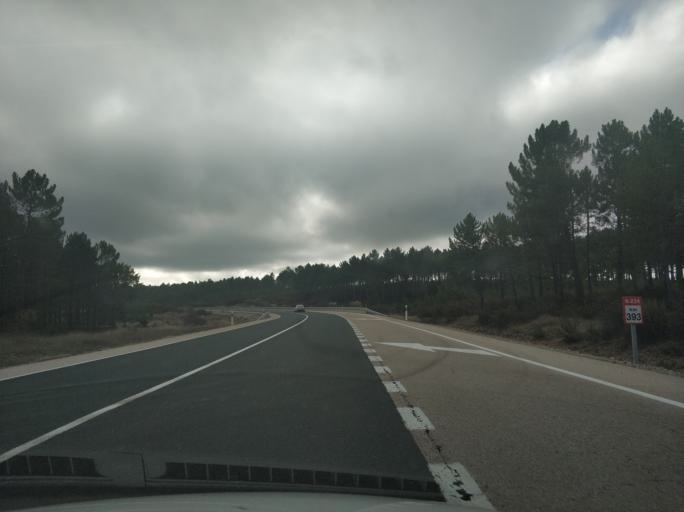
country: ES
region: Castille and Leon
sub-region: Provincia de Soria
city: Muriel Viejo
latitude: 41.8257
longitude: -2.9450
